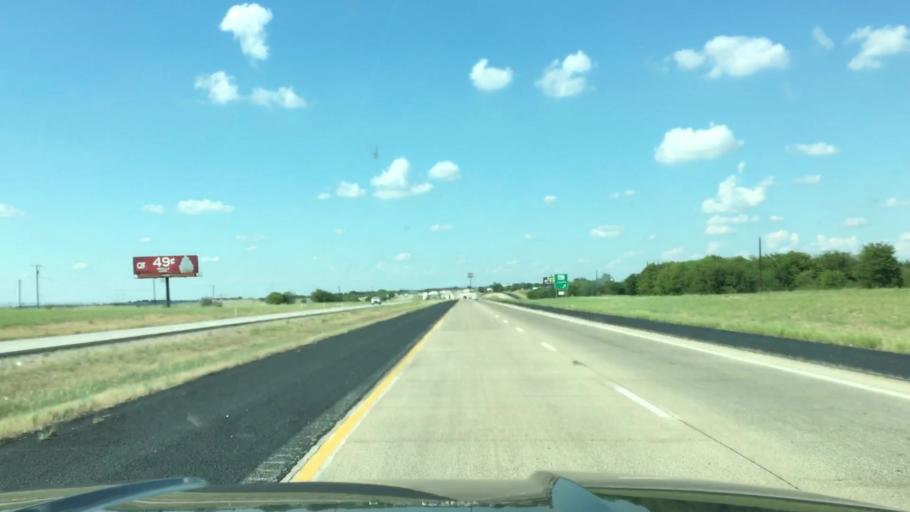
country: US
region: Texas
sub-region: Wise County
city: New Fairview
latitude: 33.0887
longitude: -97.4718
